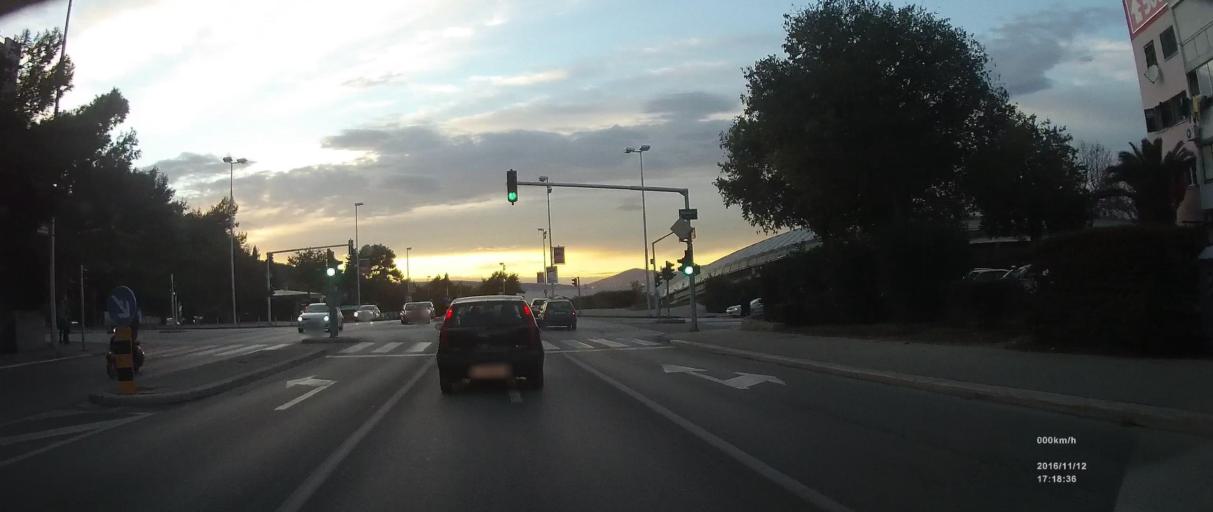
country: HR
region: Splitsko-Dalmatinska
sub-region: Grad Split
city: Split
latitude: 43.5184
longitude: 16.4351
